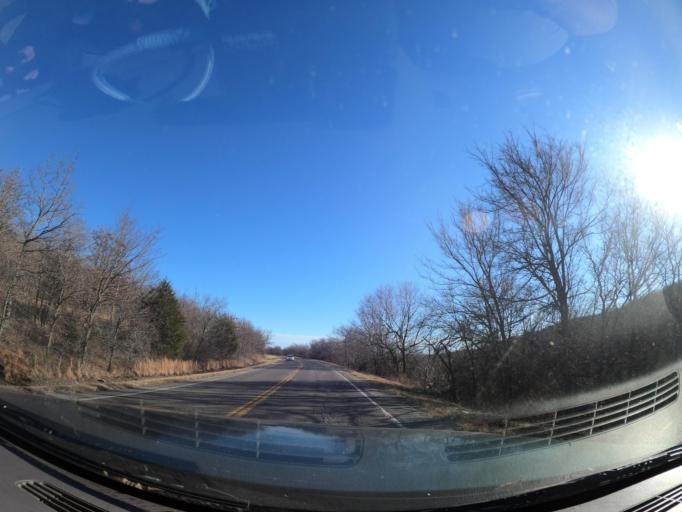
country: US
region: Oklahoma
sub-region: Pittsburg County
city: Longtown
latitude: 35.2199
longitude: -95.4280
